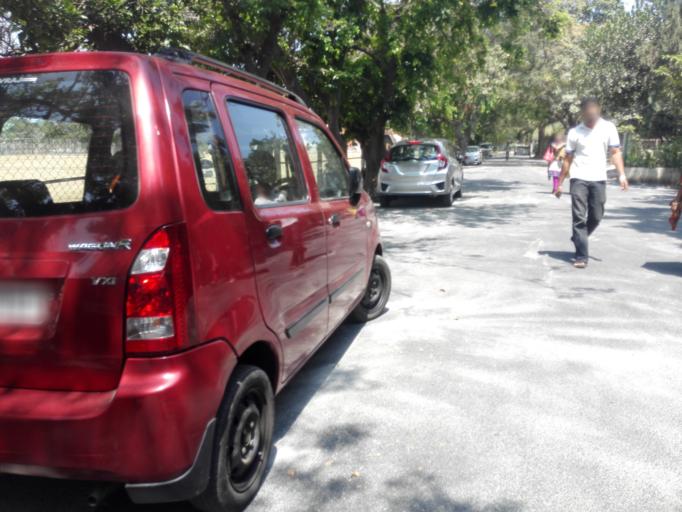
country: IN
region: Tamil Nadu
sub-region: Chennai
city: Gandhi Nagar
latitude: 13.0107
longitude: 80.2375
